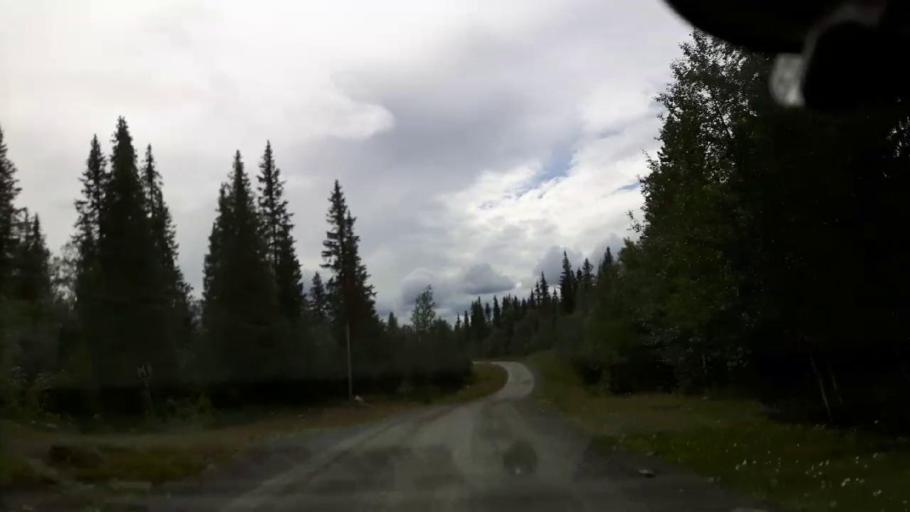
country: SE
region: Jaemtland
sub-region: Krokoms Kommun
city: Valla
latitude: 63.7381
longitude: 13.8377
